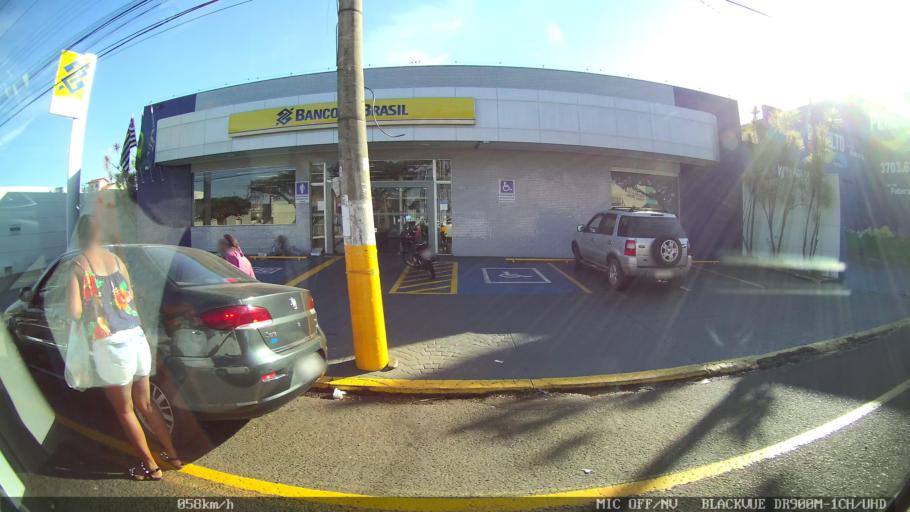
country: BR
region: Sao Paulo
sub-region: Franca
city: Franca
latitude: -20.5151
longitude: -47.3986
